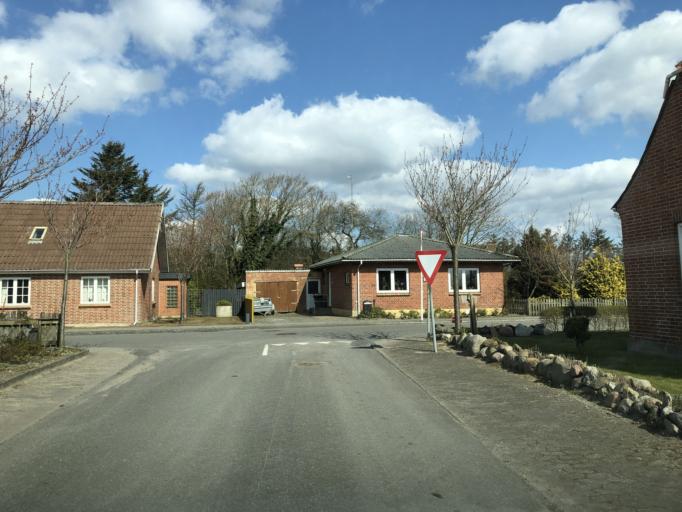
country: DK
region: Central Jutland
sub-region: Holstebro Kommune
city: Ulfborg
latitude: 56.3948
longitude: 8.2147
